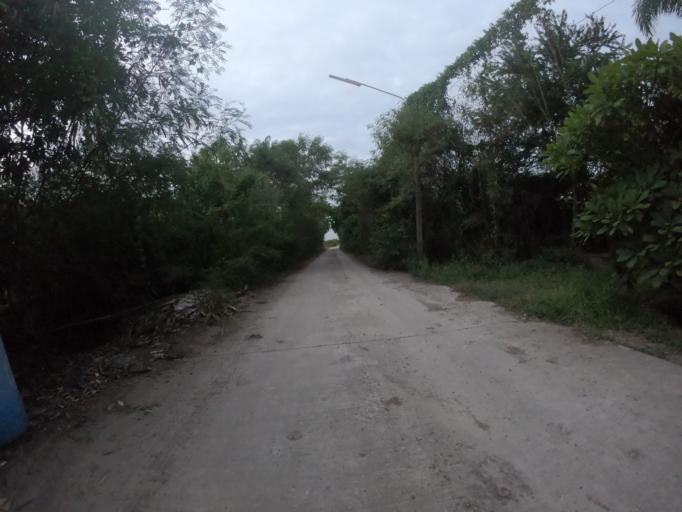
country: TH
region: Pathum Thani
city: Ban Lam Luk Ka
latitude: 14.0138
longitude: 100.8016
